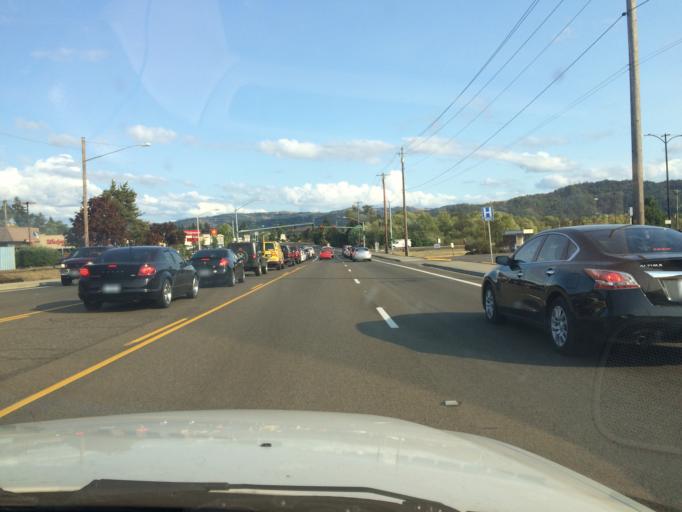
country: US
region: Oregon
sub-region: Douglas County
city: Roseburg
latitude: 43.2329
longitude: -123.3744
